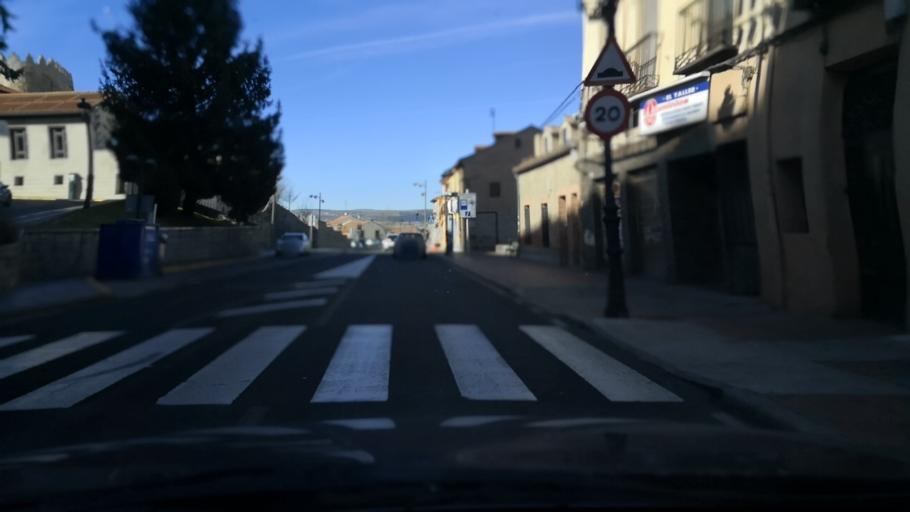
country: ES
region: Castille and Leon
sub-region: Provincia de Avila
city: Avila
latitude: 40.6583
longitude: -4.6958
